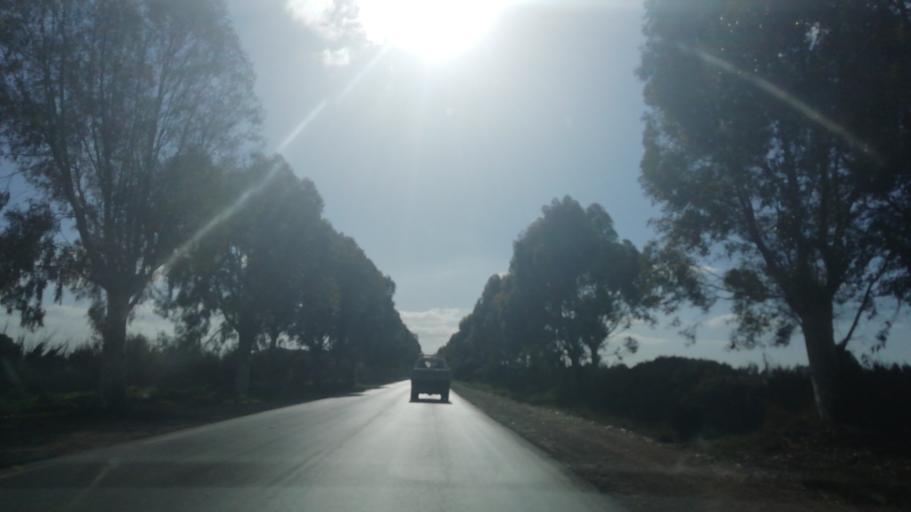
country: DZ
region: Mostaganem
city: Mostaganem
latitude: 35.9803
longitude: 0.2796
